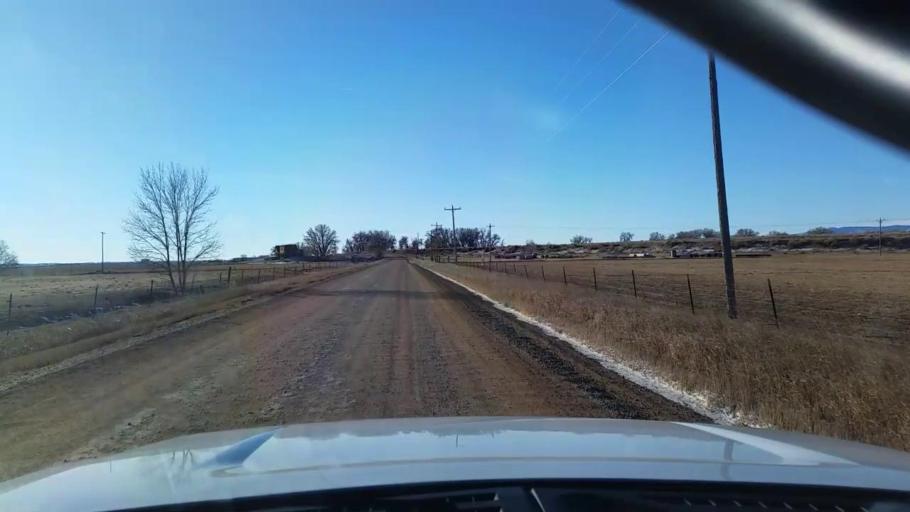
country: US
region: Colorado
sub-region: Larimer County
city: Wellington
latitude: 40.7637
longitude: -105.0380
